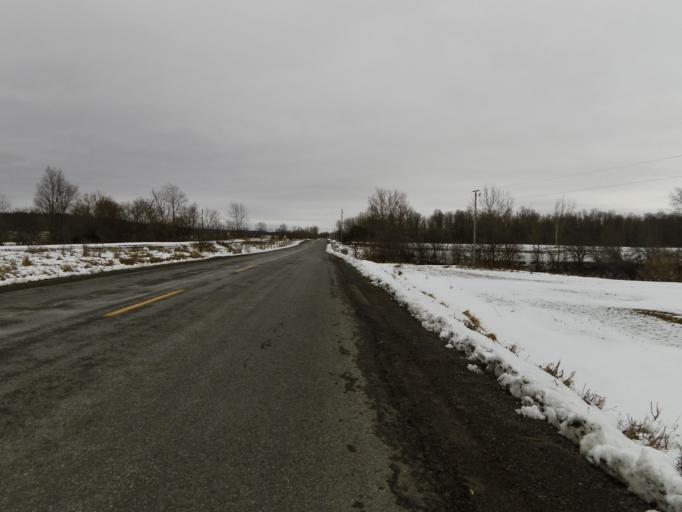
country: CA
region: Ontario
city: Carleton Place
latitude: 45.2781
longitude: -76.2427
